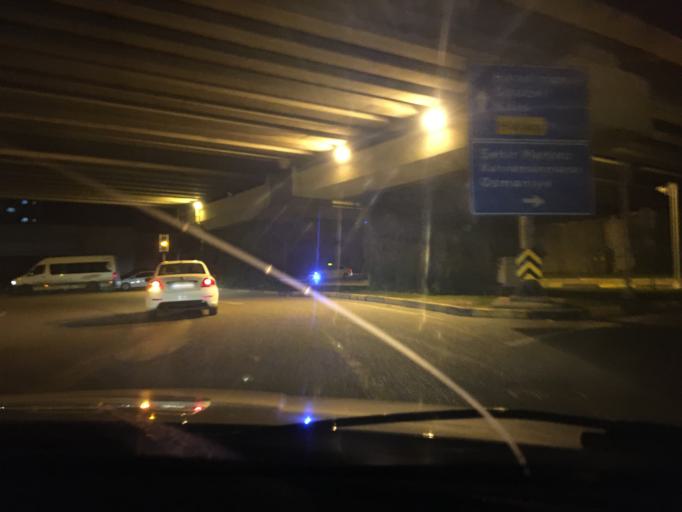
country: TR
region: Gaziantep
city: Gaziantep
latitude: 37.0805
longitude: 37.4147
